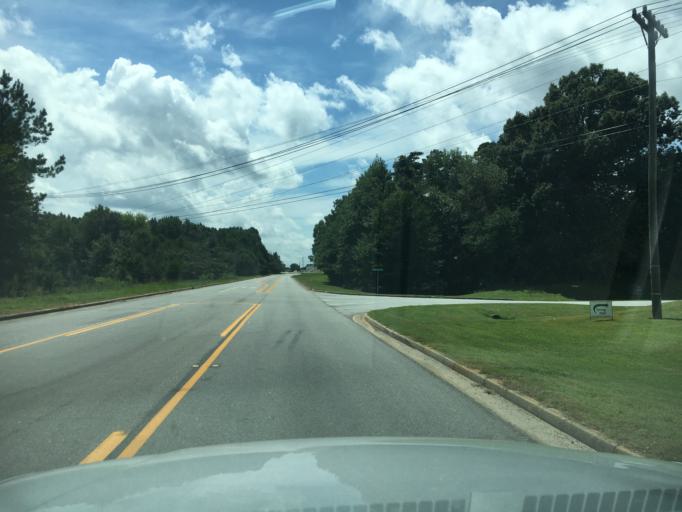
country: US
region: South Carolina
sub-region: Greenville County
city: Gantt
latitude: 34.7911
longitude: -82.4114
